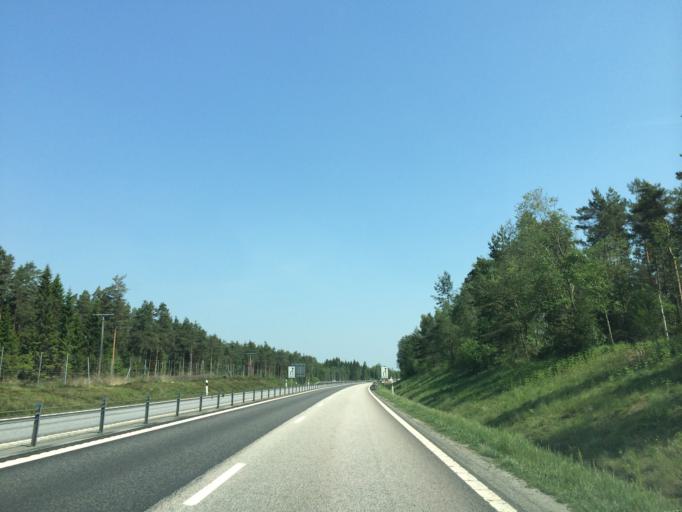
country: SE
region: Kronoberg
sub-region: Ljungby Kommun
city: Ljungby
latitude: 56.8343
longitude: 13.9102
